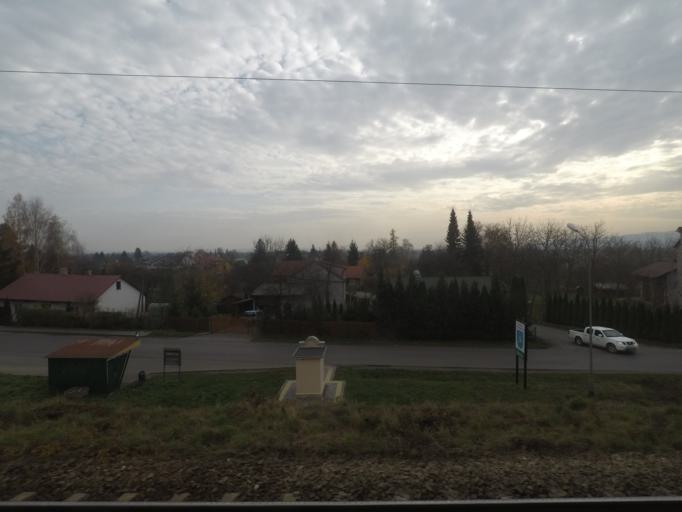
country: PL
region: Subcarpathian Voivodeship
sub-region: Powiat przemyski
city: Zurawica
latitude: 49.8023
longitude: 22.7970
